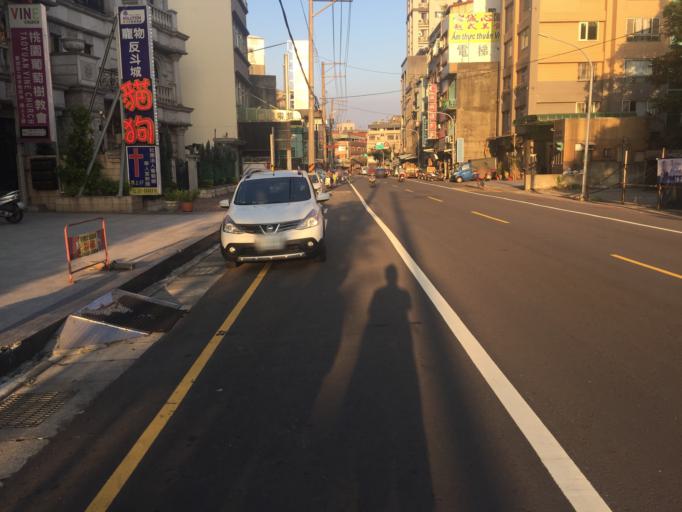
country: TW
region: Taiwan
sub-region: Taoyuan
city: Taoyuan
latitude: 24.9881
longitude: 121.3160
